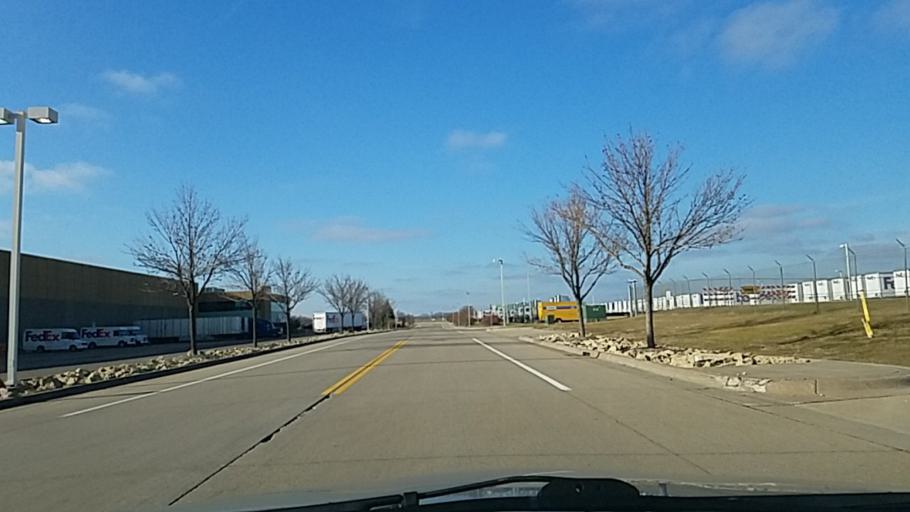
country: US
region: Minnesota
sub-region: Hennepin County
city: Richfield
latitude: 44.8831
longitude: -93.2312
